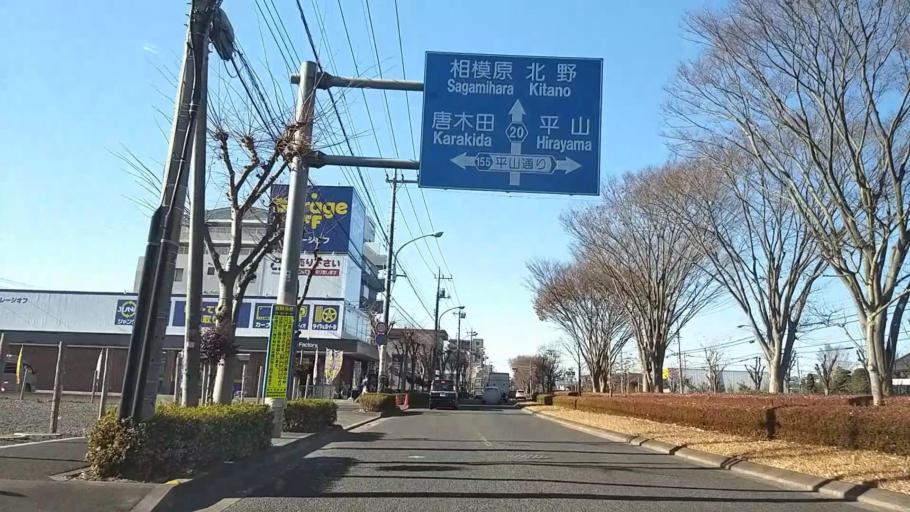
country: JP
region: Tokyo
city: Hino
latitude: 35.6282
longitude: 139.3996
